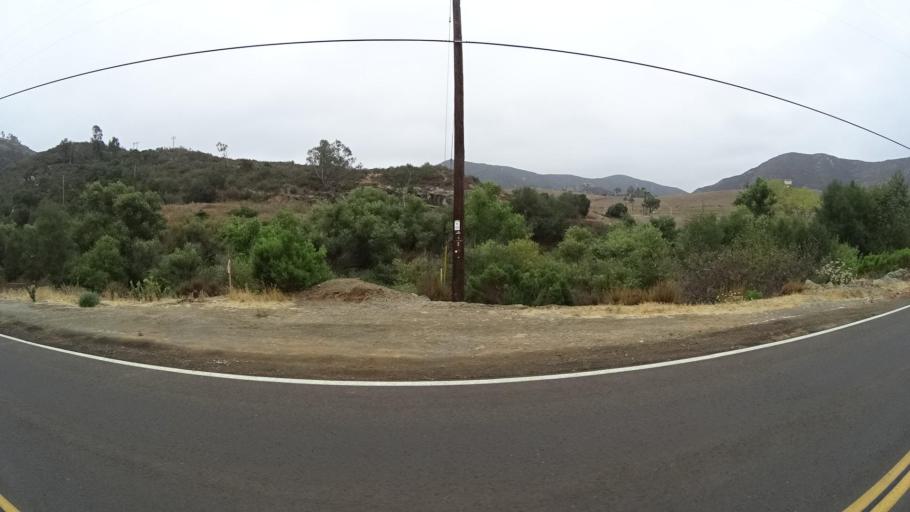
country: US
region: California
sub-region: San Diego County
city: Escondido
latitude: 33.0993
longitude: -117.1288
